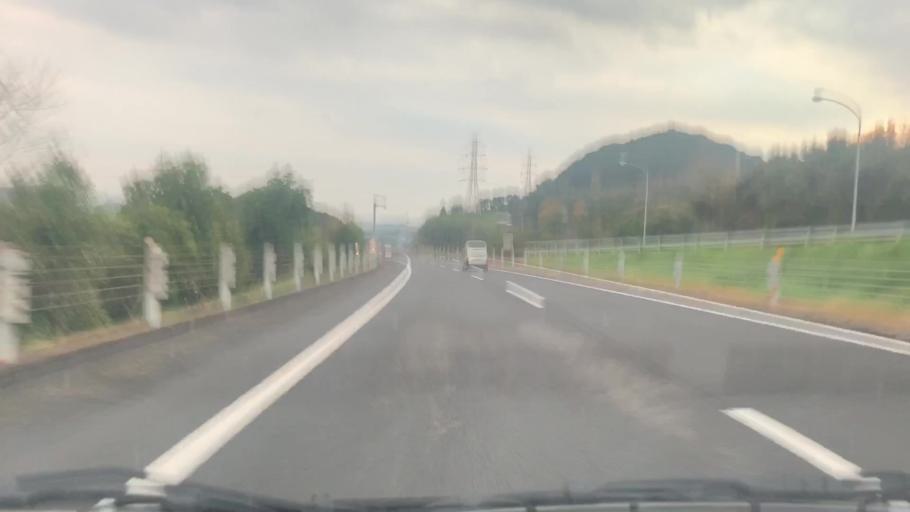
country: JP
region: Nagasaki
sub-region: Isahaya-shi
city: Isahaya
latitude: 32.8601
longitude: 130.0030
